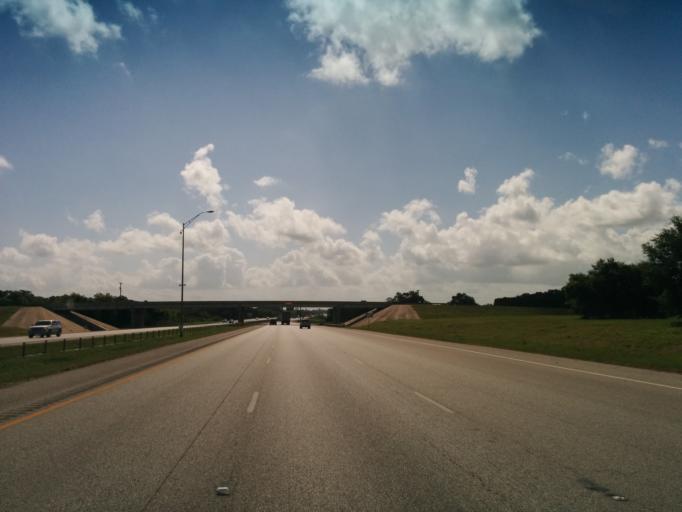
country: US
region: Texas
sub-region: Colorado County
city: Columbus
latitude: 29.6936
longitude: -96.5645
